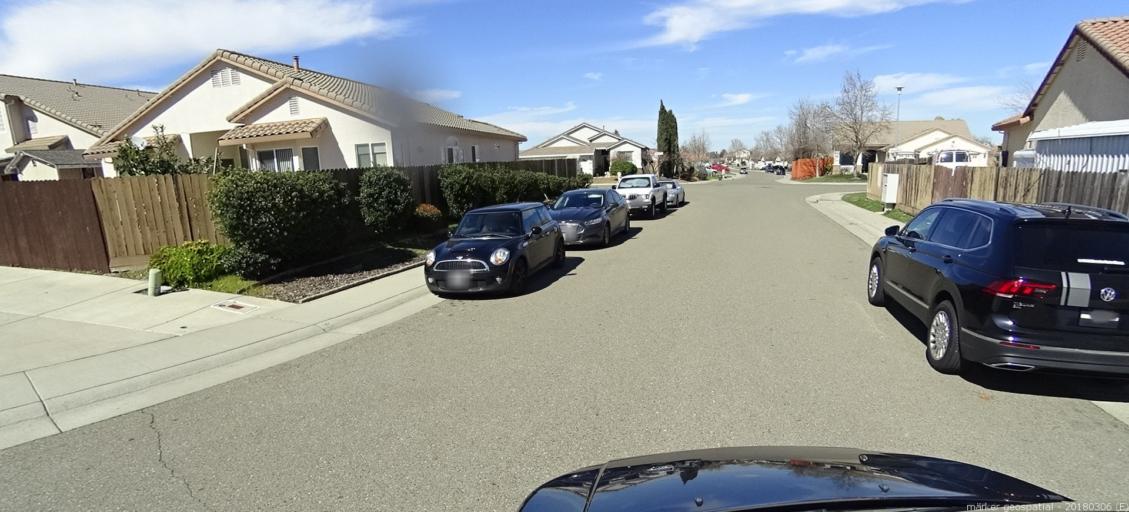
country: US
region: California
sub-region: Sacramento County
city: Vineyard
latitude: 38.4681
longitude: -121.3583
